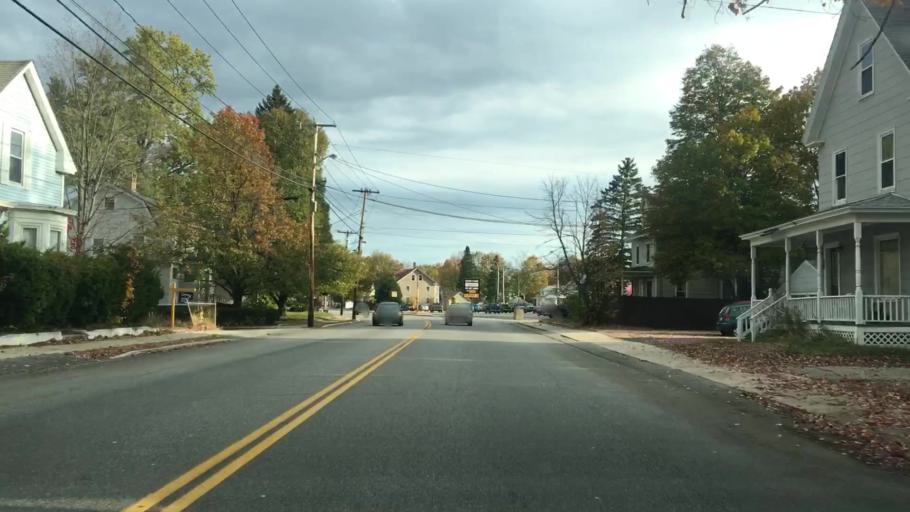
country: US
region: Maine
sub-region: York County
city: Sanford (historical)
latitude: 43.4452
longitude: -70.7852
